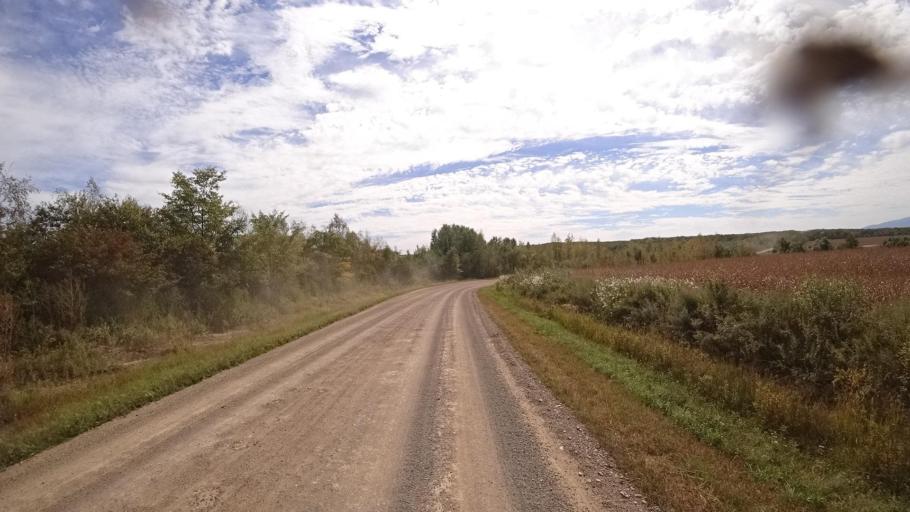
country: RU
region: Primorskiy
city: Yakovlevka
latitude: 44.5632
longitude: 133.5959
